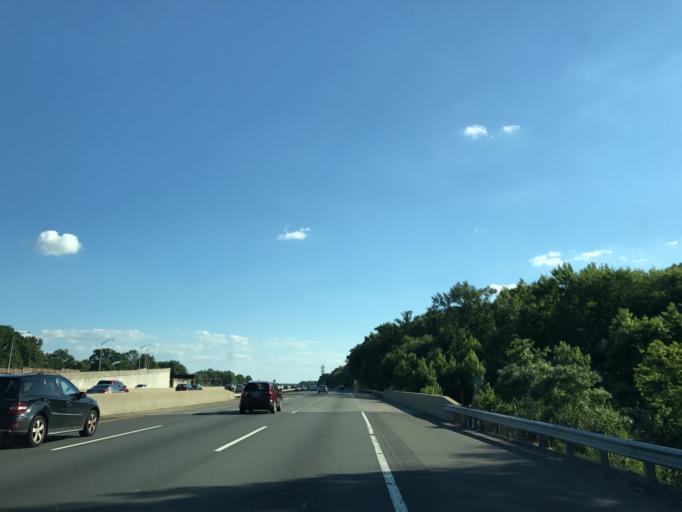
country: US
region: New Jersey
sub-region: Middlesex County
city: East Brunswick
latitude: 40.4243
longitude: -74.4413
